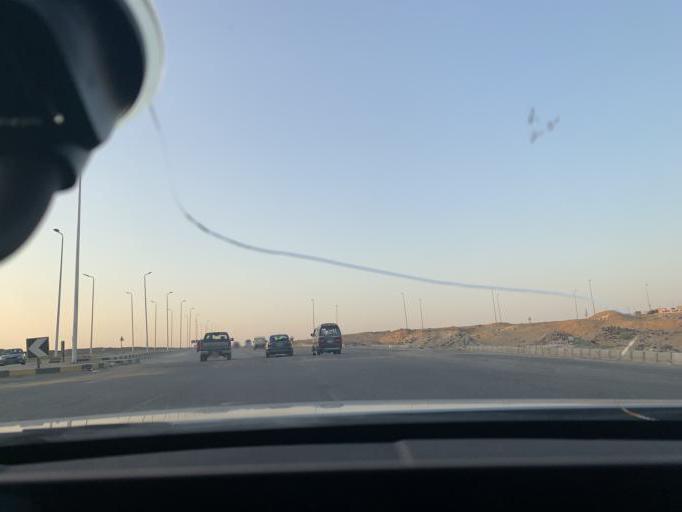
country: EG
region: Muhafazat al Qahirah
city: Halwan
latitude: 29.9839
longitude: 31.4689
